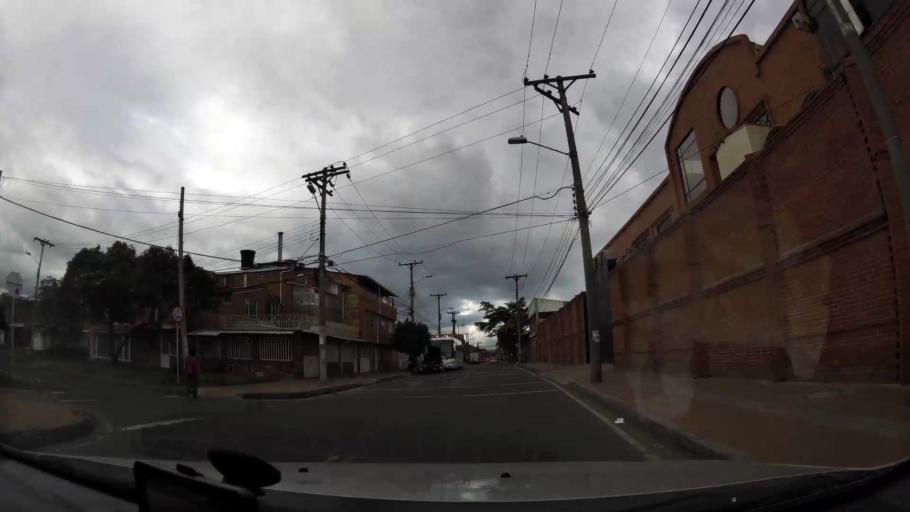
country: CO
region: Bogota D.C.
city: Bogota
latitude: 4.6006
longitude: -74.1385
